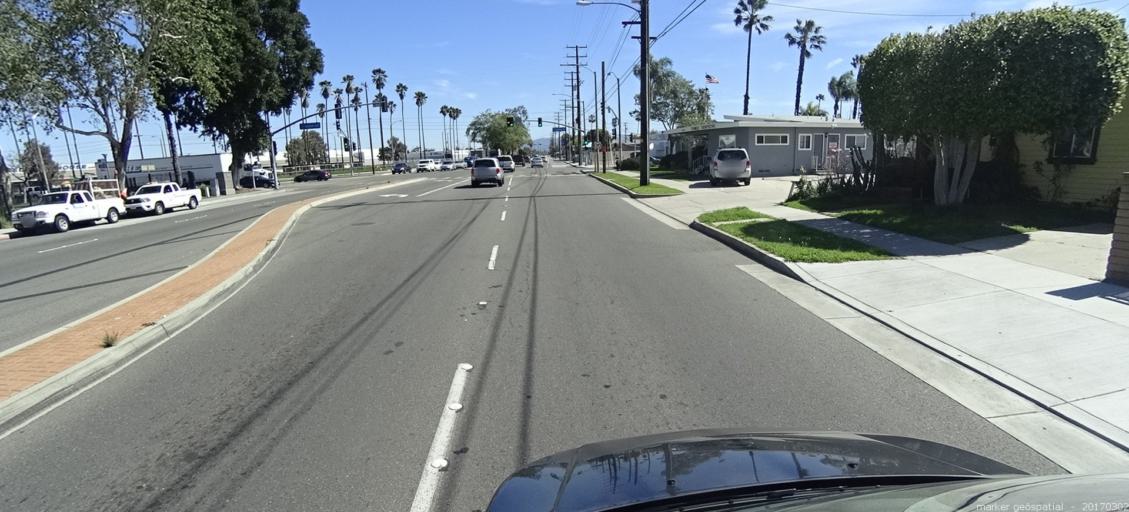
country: US
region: California
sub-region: Orange County
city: Anaheim
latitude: 33.8472
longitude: -117.9207
